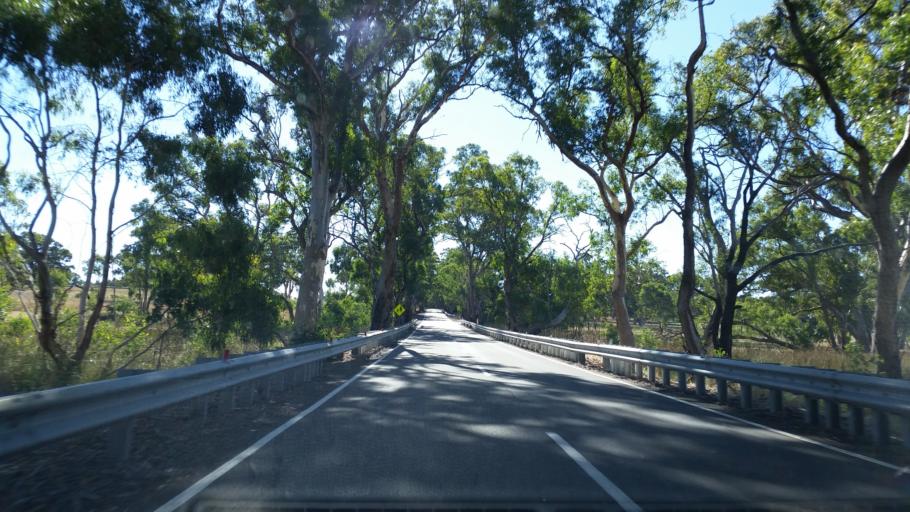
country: AU
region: South Australia
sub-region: Adelaide Hills
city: Birdwood
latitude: -34.8135
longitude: 139.0377
